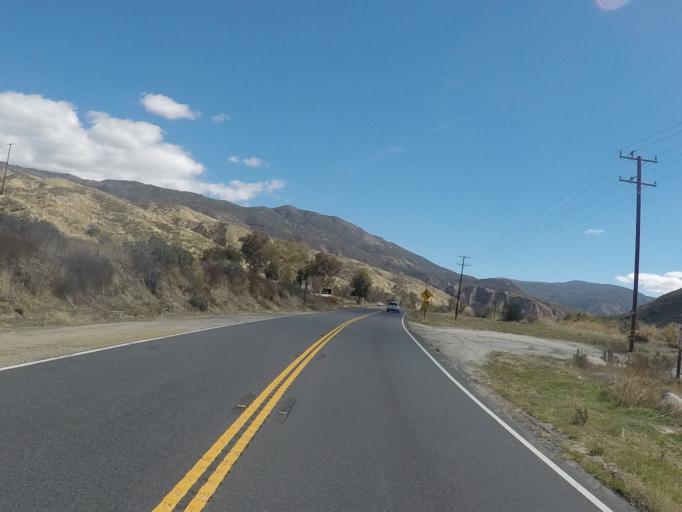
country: US
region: California
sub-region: Riverside County
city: Valle Vista
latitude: 33.7369
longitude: -116.8216
